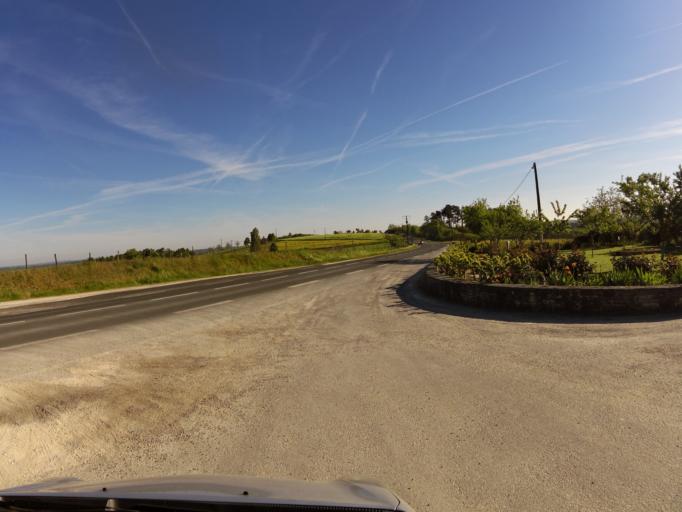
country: FR
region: Aquitaine
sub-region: Departement de la Dordogne
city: Sarlat-la-Caneda
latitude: 44.9444
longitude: 1.2203
